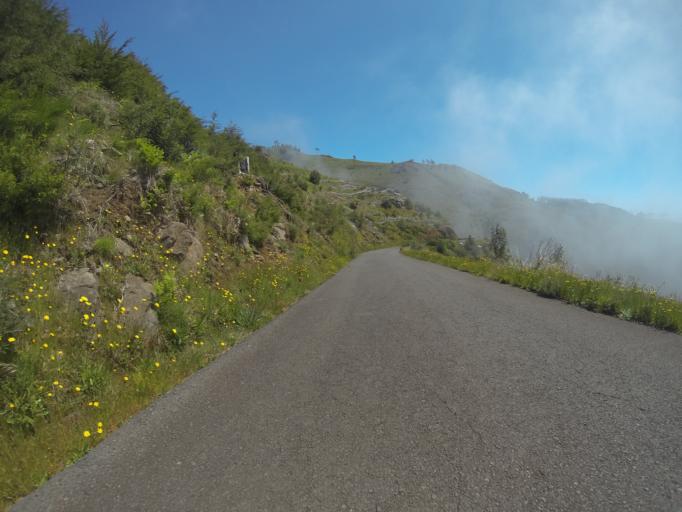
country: PT
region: Madeira
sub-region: Funchal
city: Nossa Senhora do Monte
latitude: 32.7009
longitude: -16.9106
